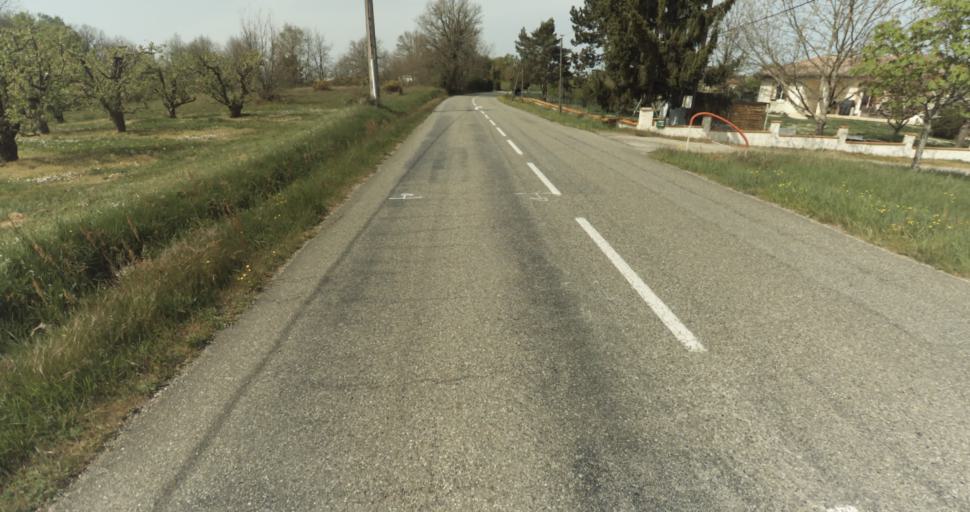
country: FR
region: Midi-Pyrenees
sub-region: Departement du Tarn-et-Garonne
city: Moissac
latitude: 44.1665
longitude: 1.0884
